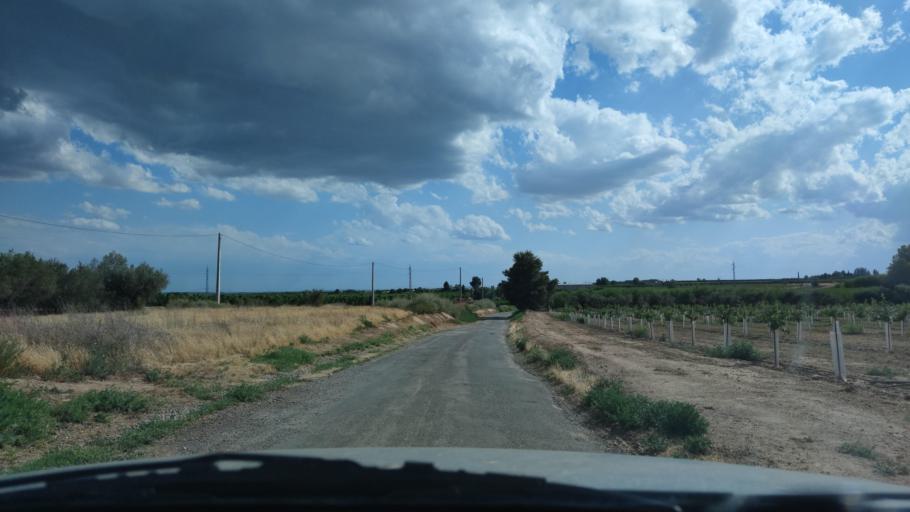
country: ES
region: Catalonia
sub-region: Provincia de Lleida
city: Alcarras
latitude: 41.5884
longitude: 0.5381
